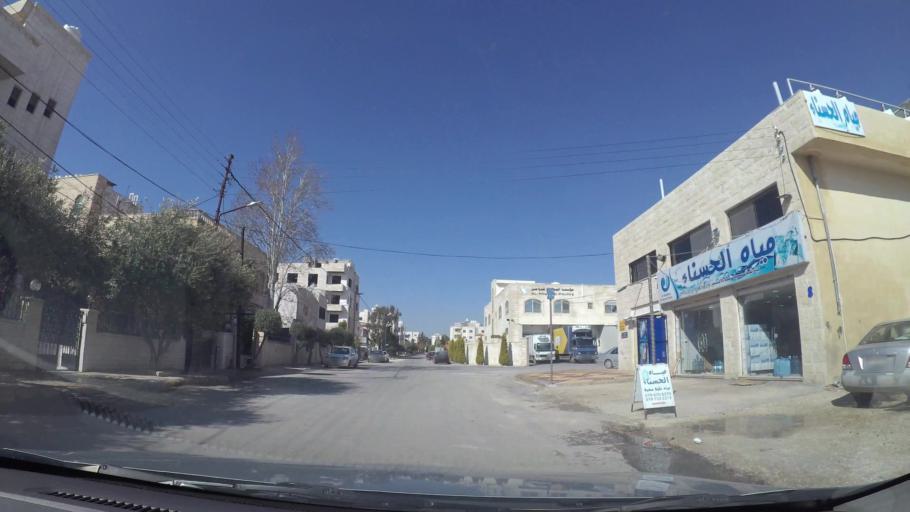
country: JO
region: Amman
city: Al Bunayyat ash Shamaliyah
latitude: 31.9034
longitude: 35.8911
